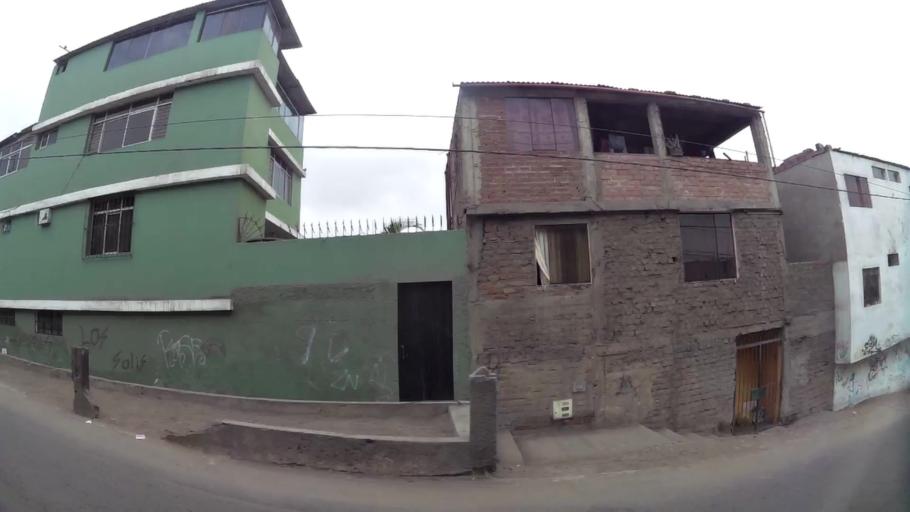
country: PE
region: Lima
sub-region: Lima
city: Surco
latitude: -12.1436
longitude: -76.9719
